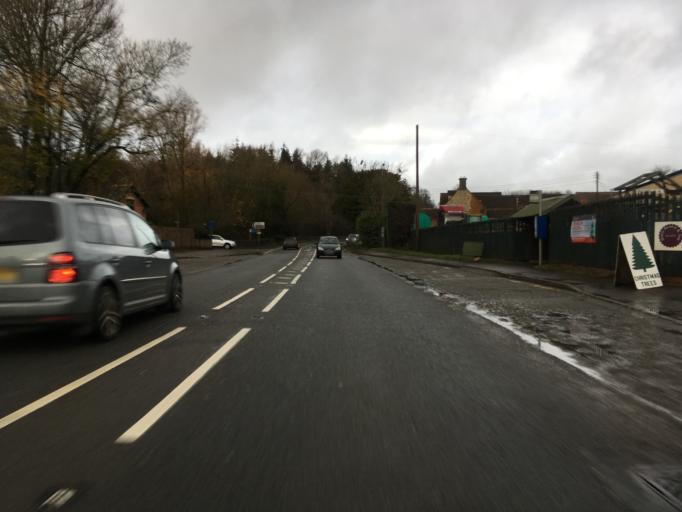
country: GB
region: England
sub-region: Gloucestershire
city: Nailsworth
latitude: 51.7184
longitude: -2.2300
